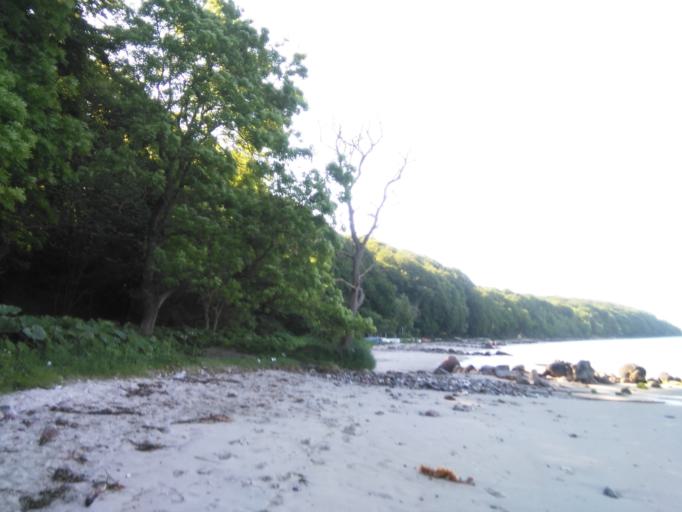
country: DK
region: Central Jutland
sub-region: Arhus Kommune
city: Beder
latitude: 56.0989
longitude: 10.2412
